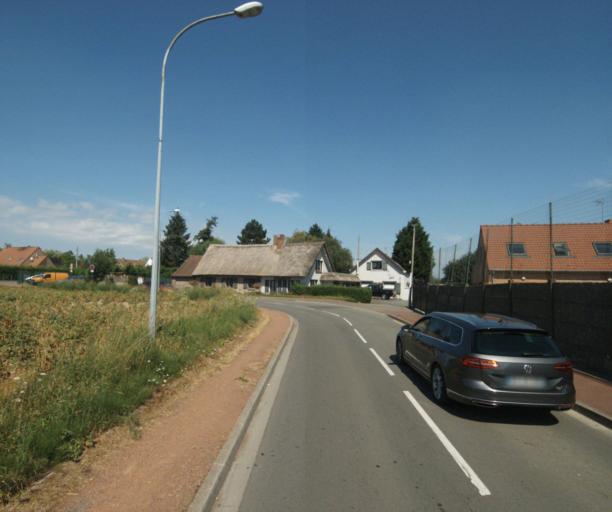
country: FR
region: Nord-Pas-de-Calais
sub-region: Departement du Nord
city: Halluin
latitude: 50.7723
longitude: 3.1471
